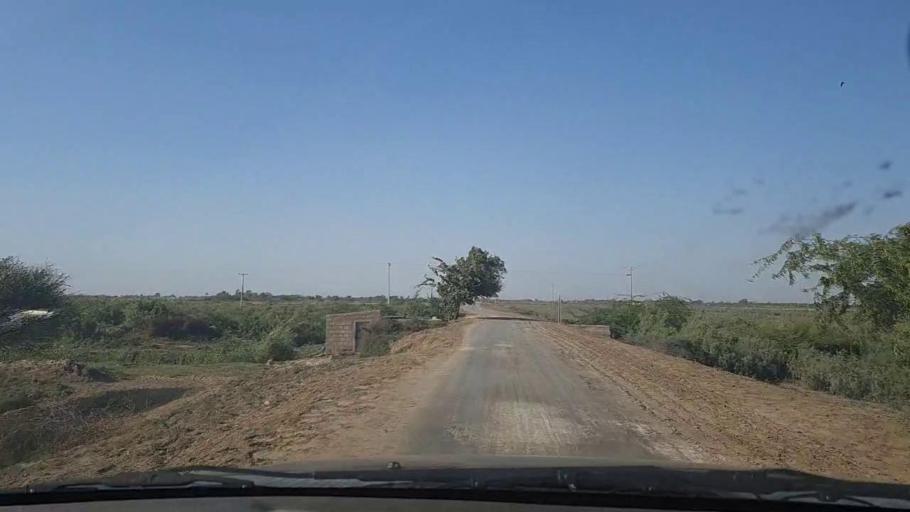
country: PK
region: Sindh
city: Chuhar Jamali
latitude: 24.3108
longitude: 67.7547
